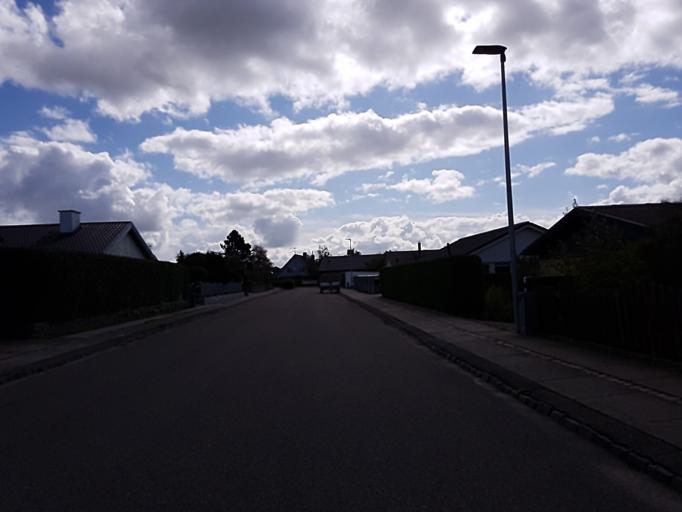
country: DK
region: Capital Region
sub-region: Egedal Kommune
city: Olstykke
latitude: 55.7899
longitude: 12.1443
